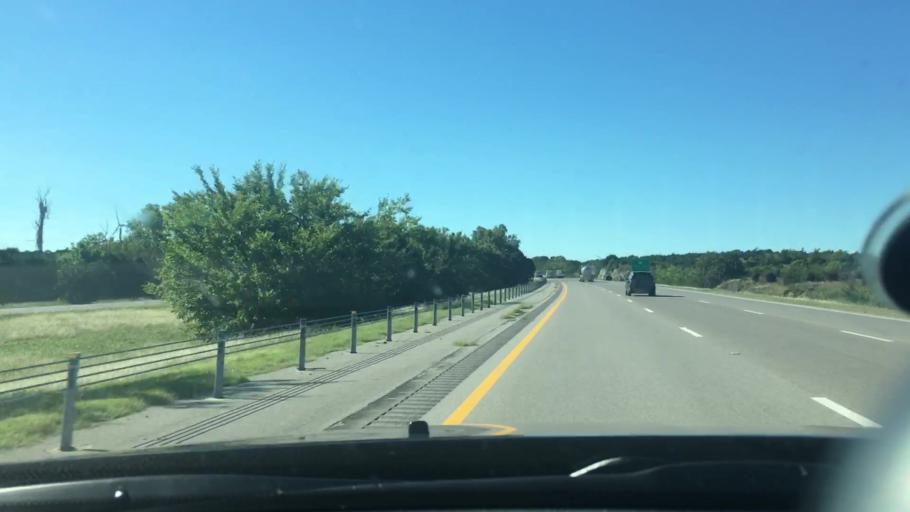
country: US
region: Oklahoma
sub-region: Murray County
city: Davis
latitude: 34.4190
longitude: -97.1367
